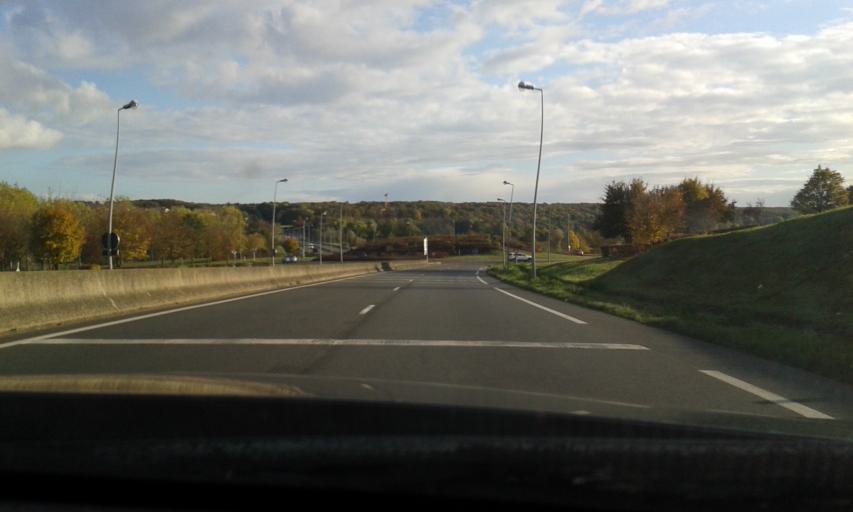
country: FR
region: Centre
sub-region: Departement d'Eure-et-Loir
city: Garnay
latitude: 48.7208
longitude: 1.3474
